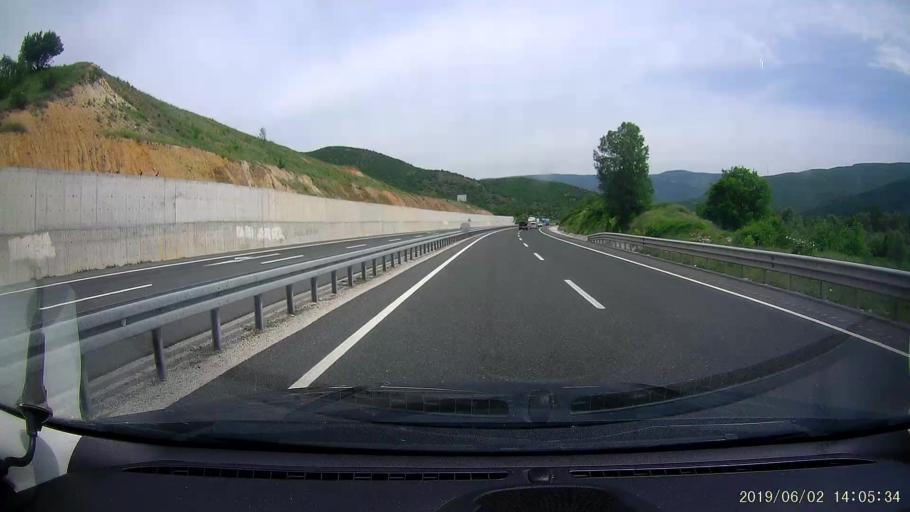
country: TR
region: Cankiri
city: Ilgaz
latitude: 40.9001
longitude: 33.6711
